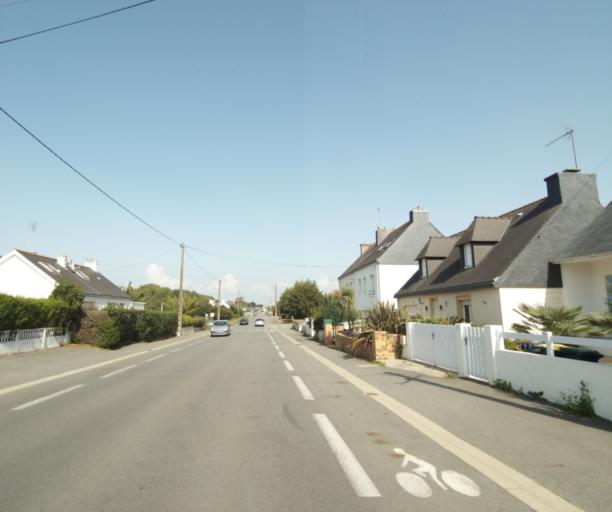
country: FR
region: Brittany
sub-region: Departement du Morbihan
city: Riantec
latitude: 47.7109
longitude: -3.3266
